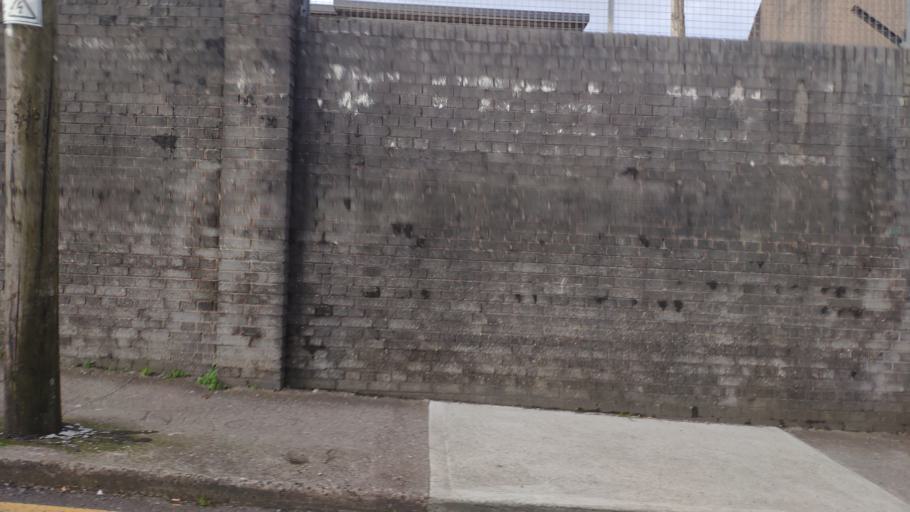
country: IE
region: Munster
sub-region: County Cork
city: Cork
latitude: 51.9055
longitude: -8.4801
